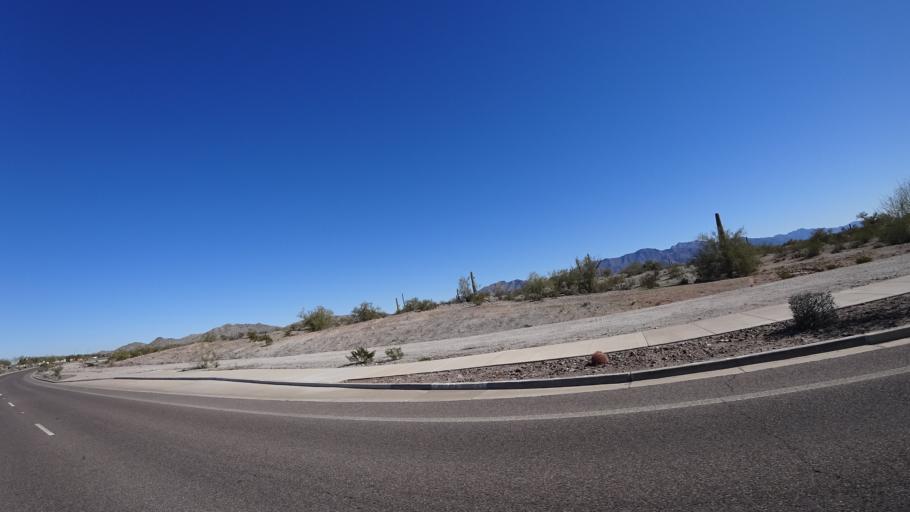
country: US
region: Arizona
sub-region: Maricopa County
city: Goodyear
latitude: 33.3142
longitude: -112.4334
